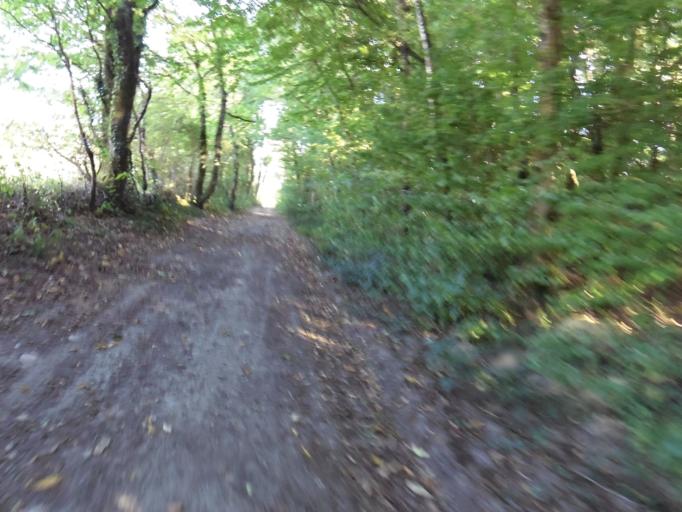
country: FR
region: Rhone-Alpes
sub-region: Departement de l'Ain
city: Perouges
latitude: 45.9175
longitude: 5.1455
